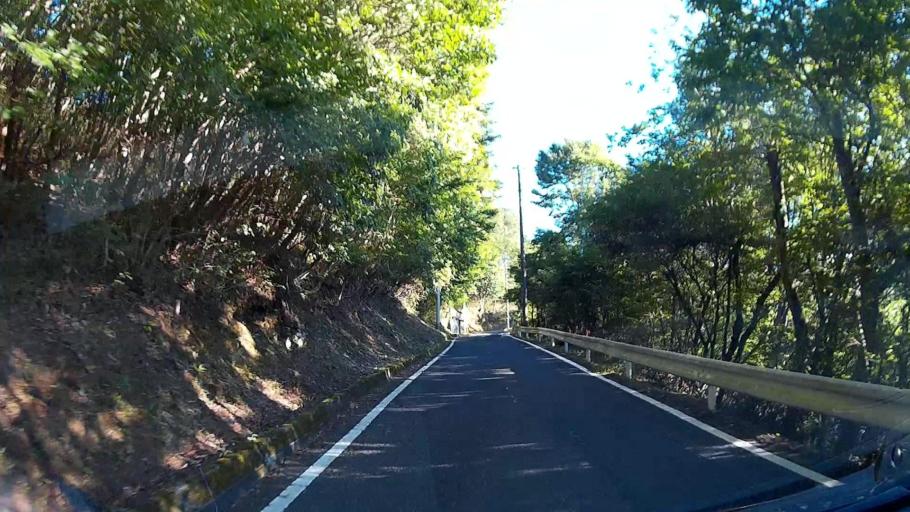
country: JP
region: Shizuoka
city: Shizuoka-shi
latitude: 35.1985
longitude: 138.2525
